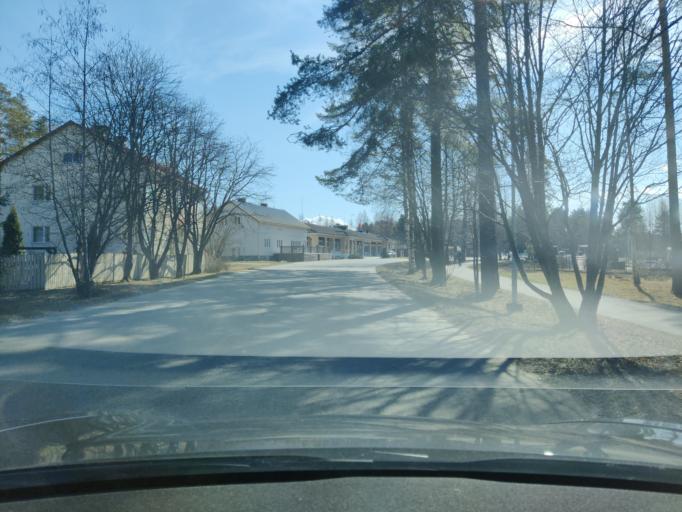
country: FI
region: Northern Savo
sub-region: Kuopio
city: Vehmersalmi
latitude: 62.7622
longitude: 28.0260
